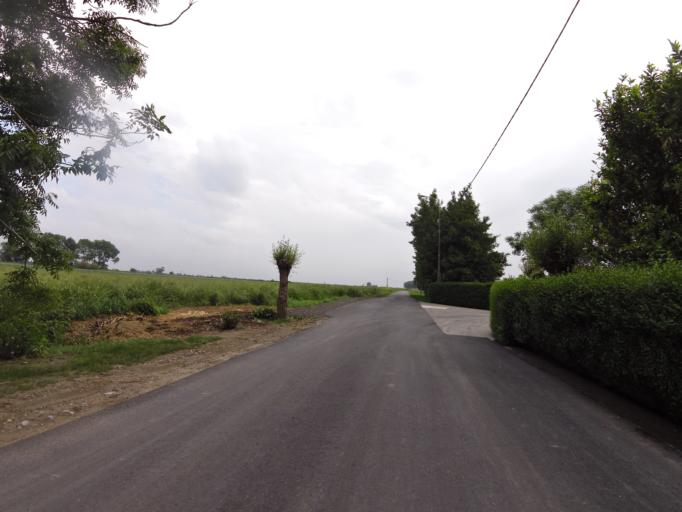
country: BE
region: Flanders
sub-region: Provincie West-Vlaanderen
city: Nieuwpoort
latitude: 51.1224
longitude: 2.8031
